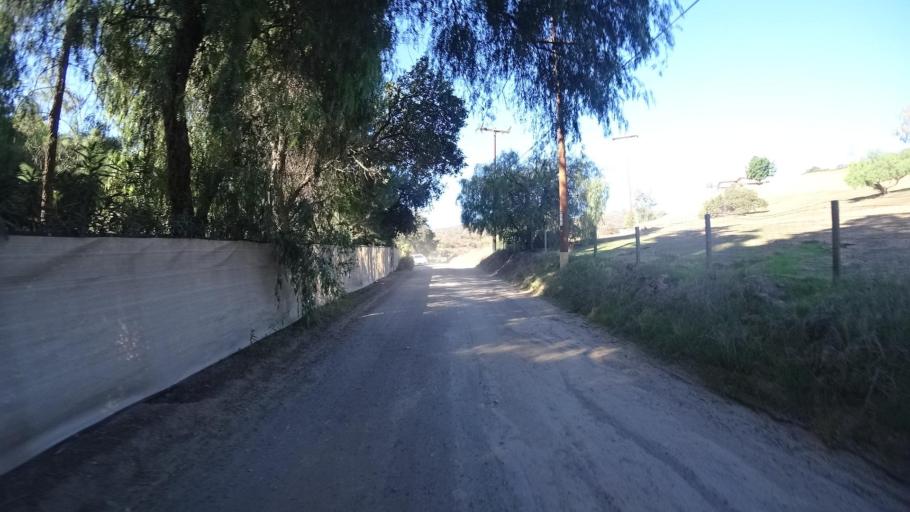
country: MX
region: Baja California
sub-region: Tijuana
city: El Nino
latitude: 32.6305
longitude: -116.7657
